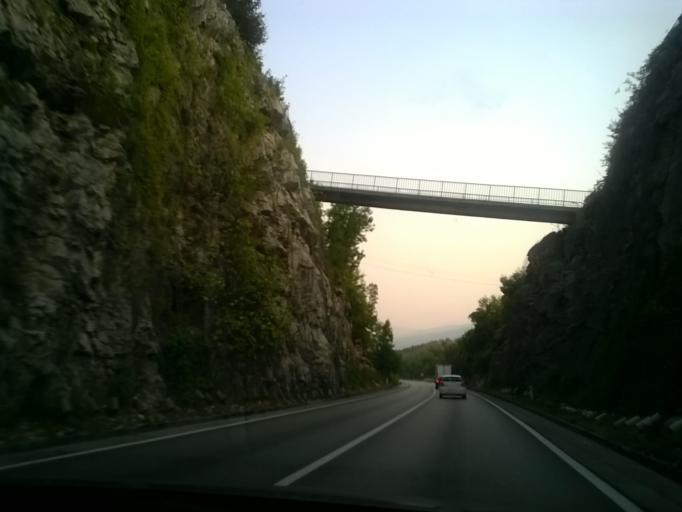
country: ME
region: Opstina Niksic
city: Niksic
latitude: 42.6911
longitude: 18.9611
